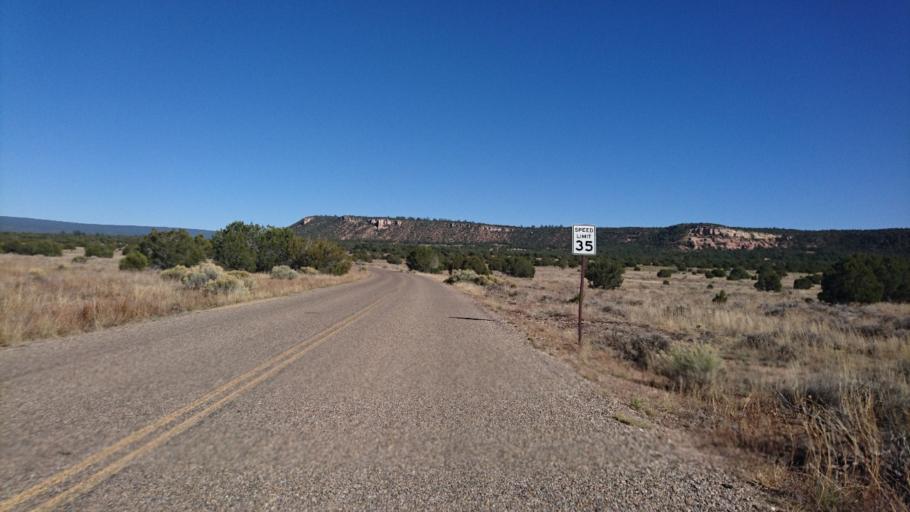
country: US
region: New Mexico
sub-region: McKinley County
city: Thoreau
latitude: 35.0368
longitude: -108.3460
